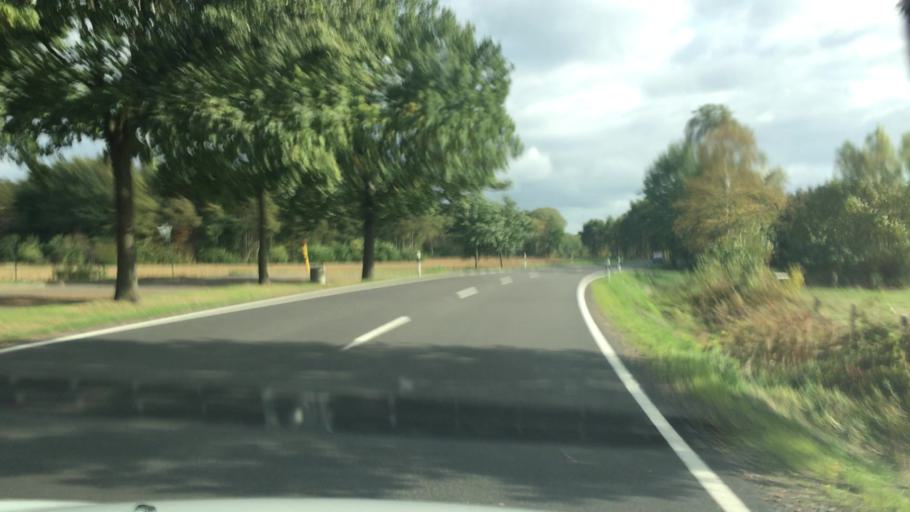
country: DE
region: Lower Saxony
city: Vechta
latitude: 52.6606
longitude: 8.3164
